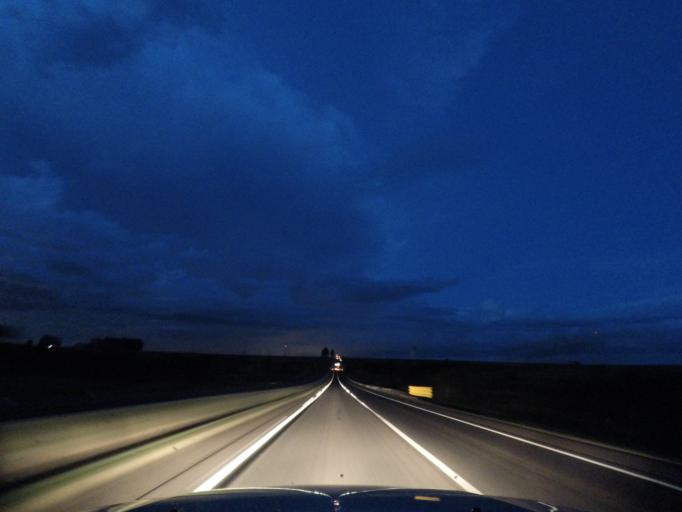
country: BR
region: Minas Gerais
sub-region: Uberlandia
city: Uberlandia
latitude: -19.2036
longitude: -48.1508
